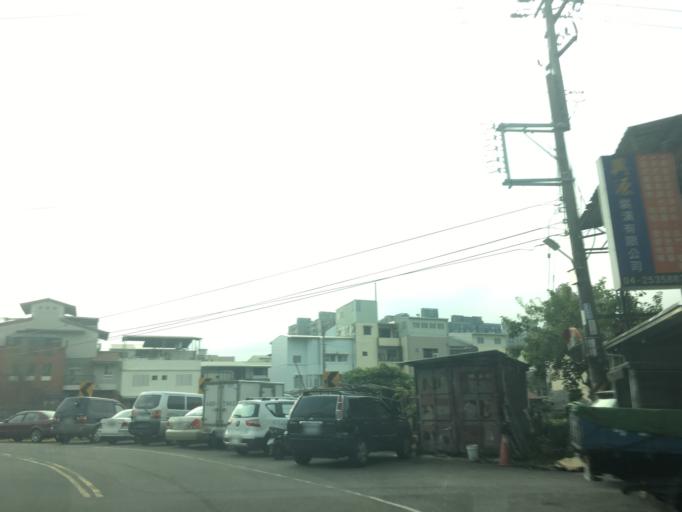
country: TW
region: Taiwan
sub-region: Taichung City
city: Taichung
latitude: 24.1920
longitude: 120.6989
